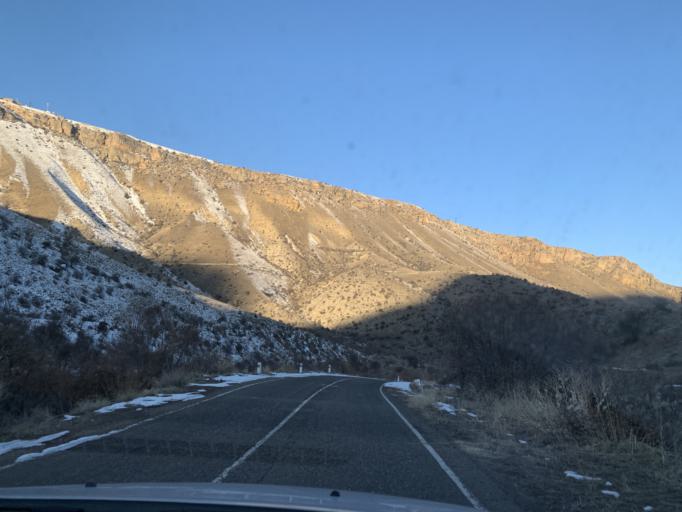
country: AM
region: Vayots' Dzori Marz
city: Areni
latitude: 39.6945
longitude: 45.2133
